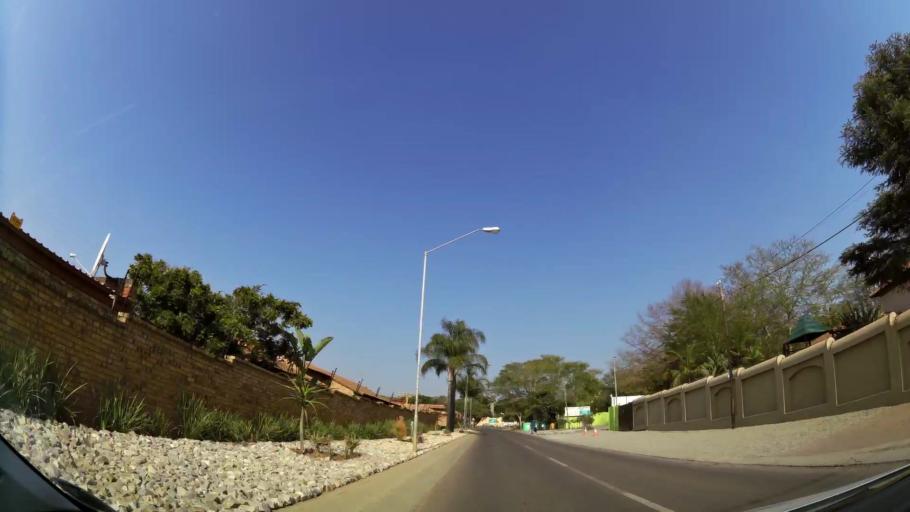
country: ZA
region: Gauteng
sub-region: City of Tshwane Metropolitan Municipality
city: Pretoria
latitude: -25.7716
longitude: 28.3362
